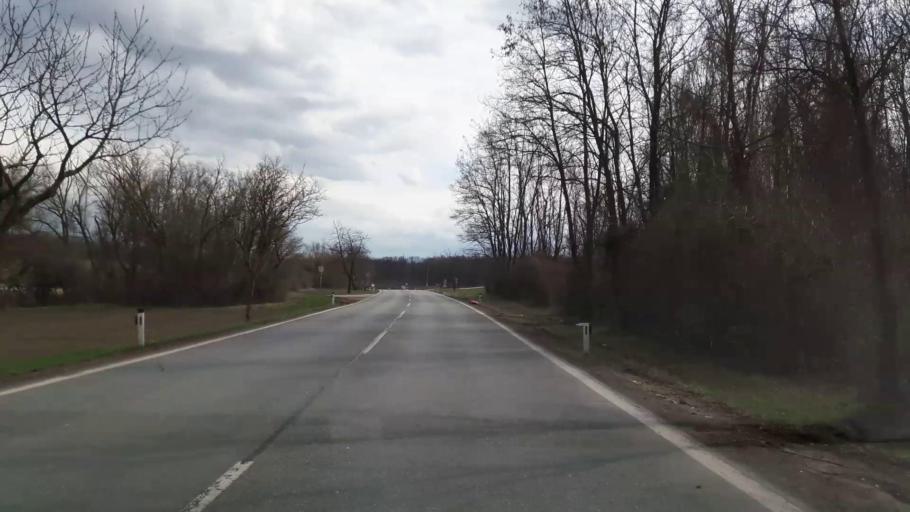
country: AT
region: Lower Austria
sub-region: Politischer Bezirk Mistelbach
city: Mistelbach
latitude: 48.5436
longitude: 16.5900
